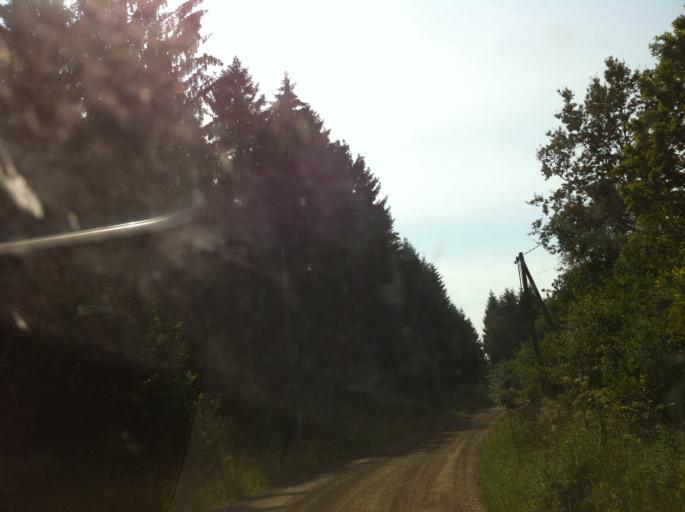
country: SE
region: Skane
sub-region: Eslovs Kommun
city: Stehag
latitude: 55.9757
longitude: 13.3889
